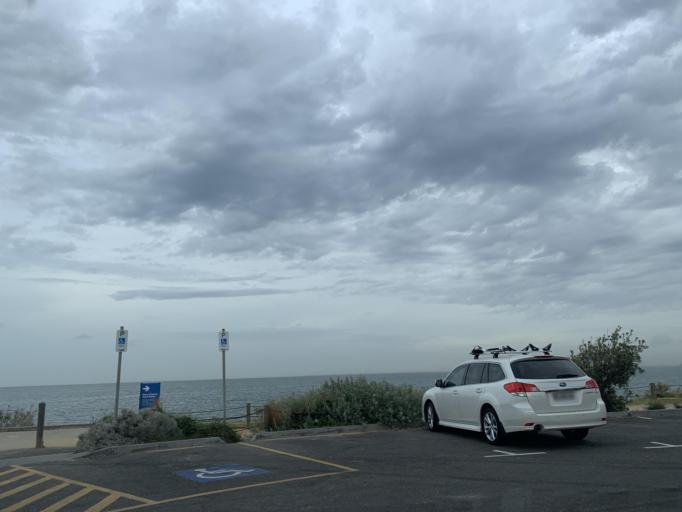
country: AU
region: Victoria
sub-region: Bayside
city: Hampton
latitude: -37.9258
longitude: 144.9860
